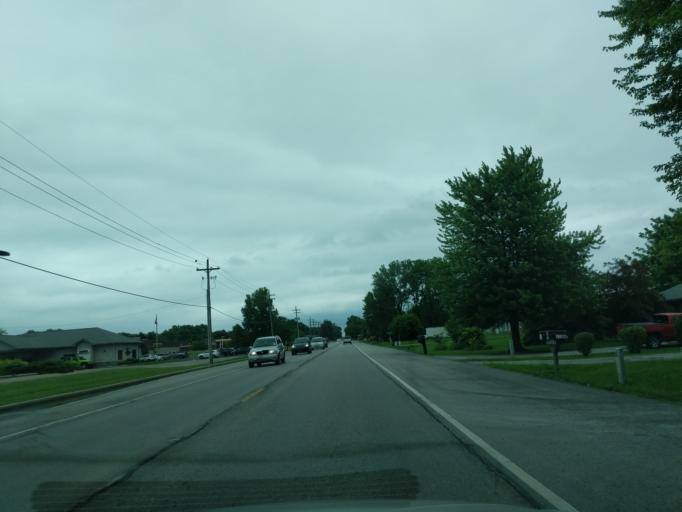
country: US
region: Indiana
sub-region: Hamilton County
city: Cicero
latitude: 40.1209
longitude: -86.0135
